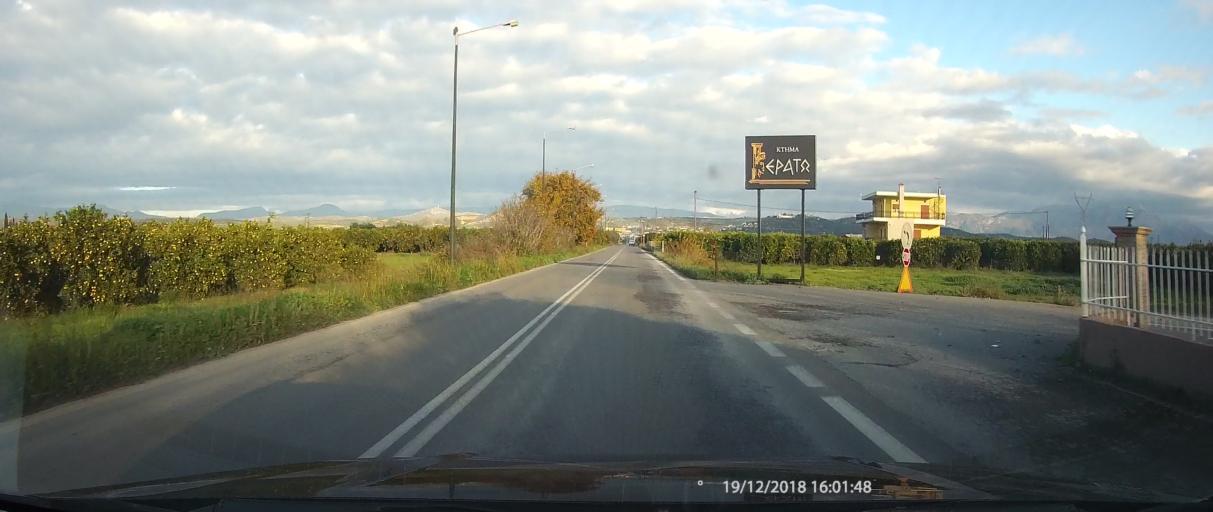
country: GR
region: Peloponnese
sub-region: Nomos Lakonias
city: Vlakhiotis
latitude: 36.8579
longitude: 22.6928
